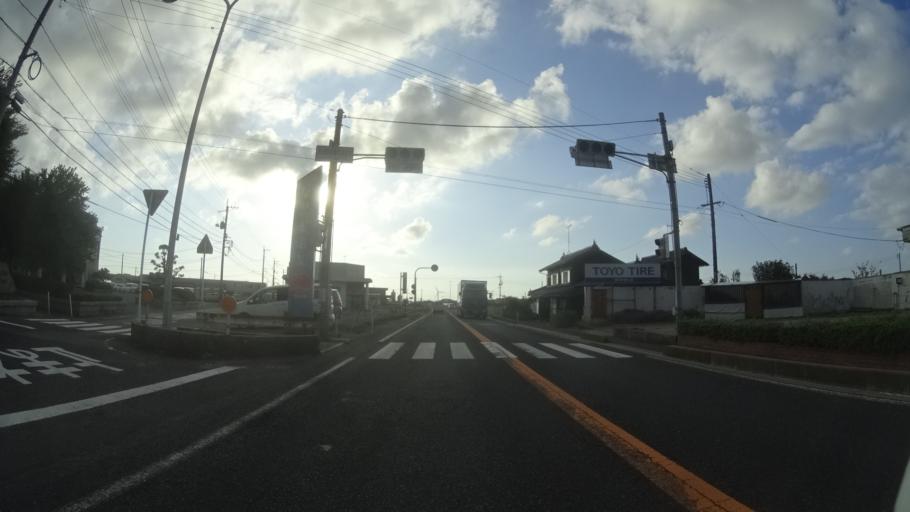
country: JP
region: Tottori
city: Kurayoshi
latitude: 35.5247
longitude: 133.5849
